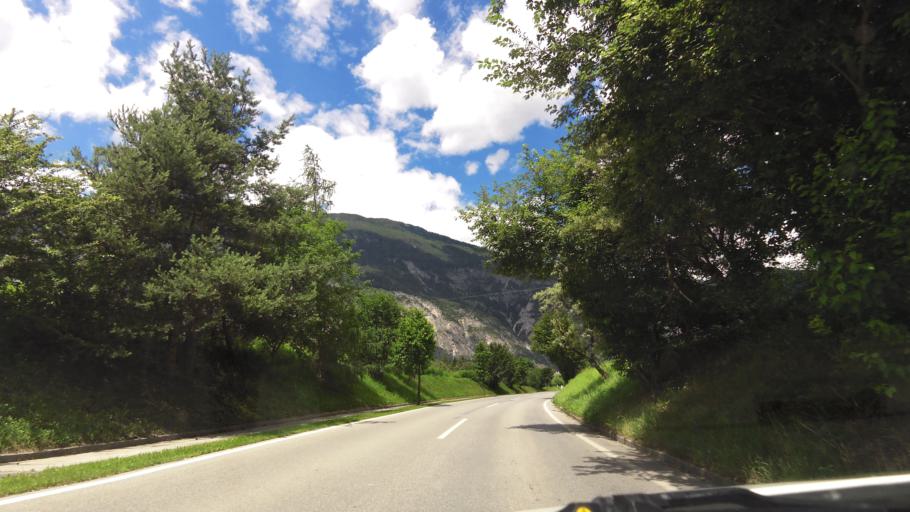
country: AT
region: Tyrol
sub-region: Politischer Bezirk Imst
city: Haiming
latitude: 47.2457
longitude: 10.8824
